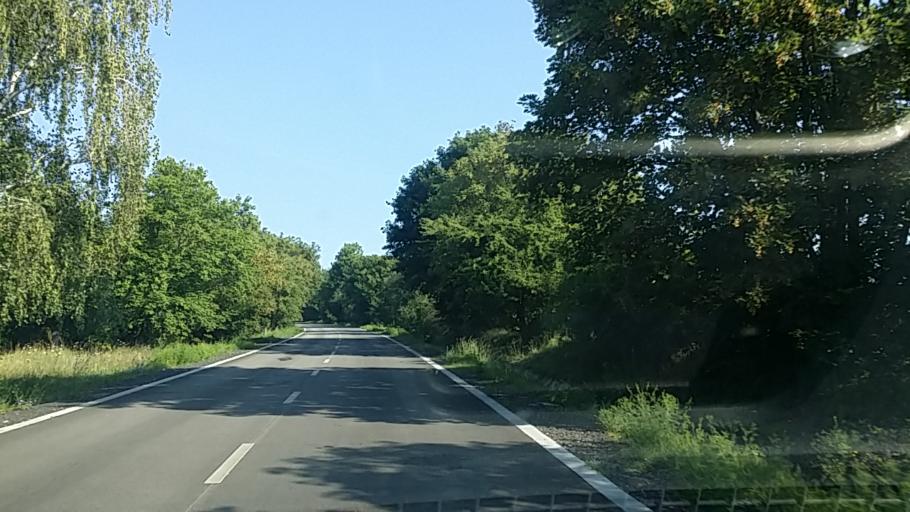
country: HU
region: Komarom-Esztergom
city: Tatabanya
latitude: 47.5790
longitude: 18.4238
